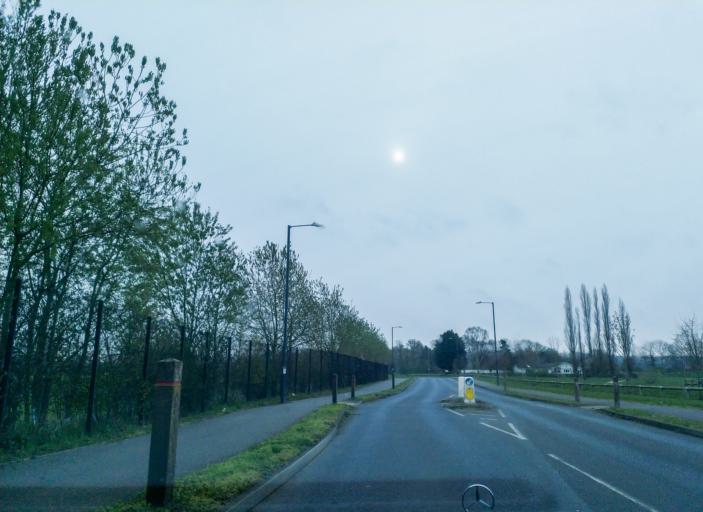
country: GB
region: England
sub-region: Warwickshire
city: Warwick
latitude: 52.2676
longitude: -1.6038
